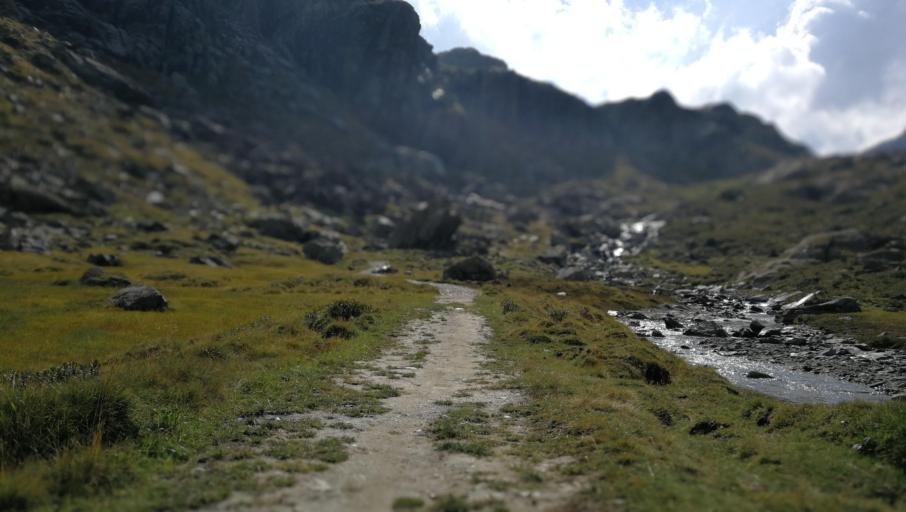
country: CH
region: Grisons
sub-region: Bernina District
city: Poschiavo
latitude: 46.3173
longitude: 9.9677
